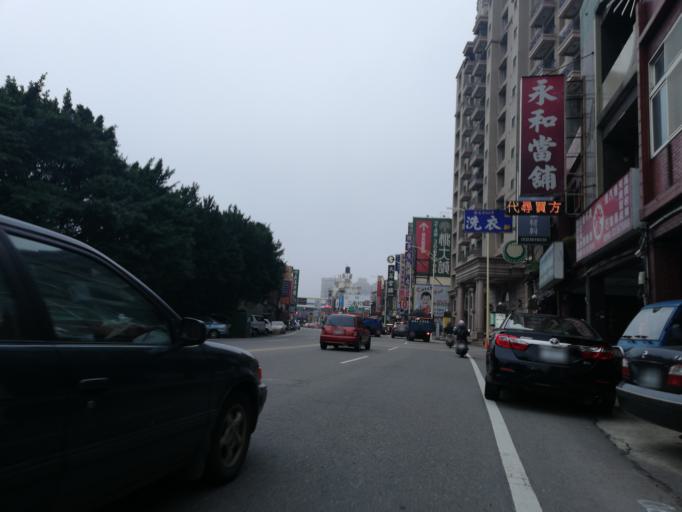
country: TW
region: Taiwan
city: Taoyuan City
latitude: 24.9765
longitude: 121.3027
